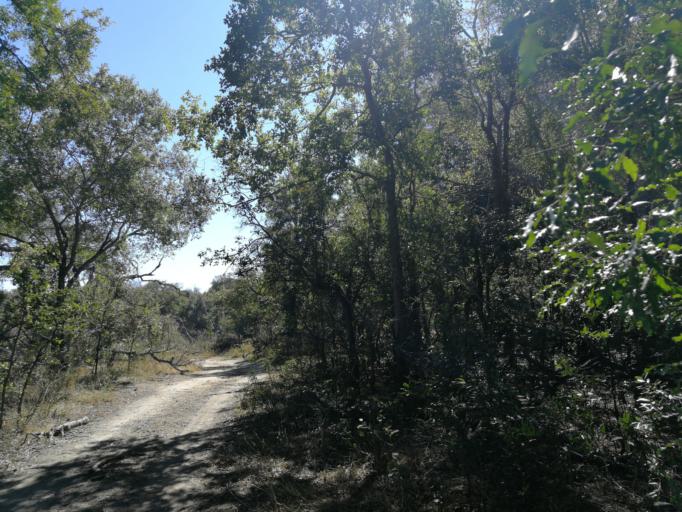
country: ZA
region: Limpopo
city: Thulamahashi
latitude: -24.9419
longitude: 31.6782
